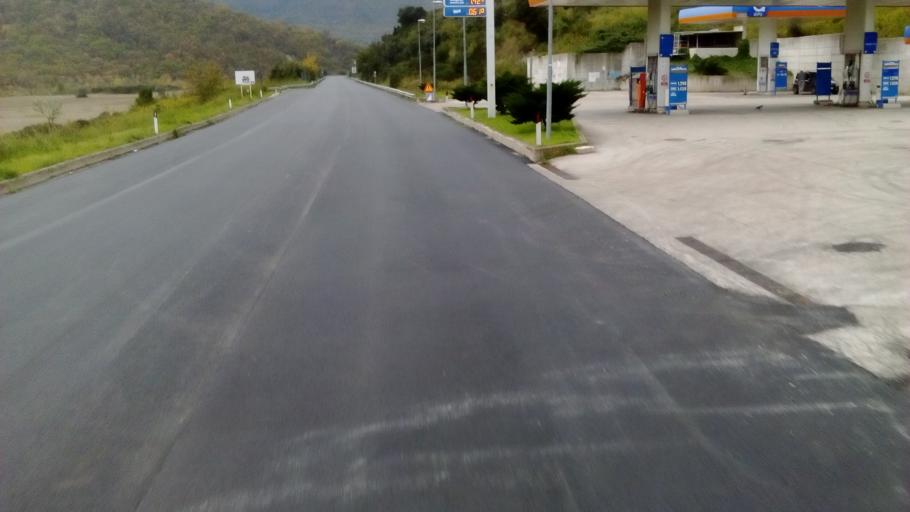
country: IT
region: Molise
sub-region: Provincia di Campobasso
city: Montemitro
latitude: 41.9186
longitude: 14.6618
